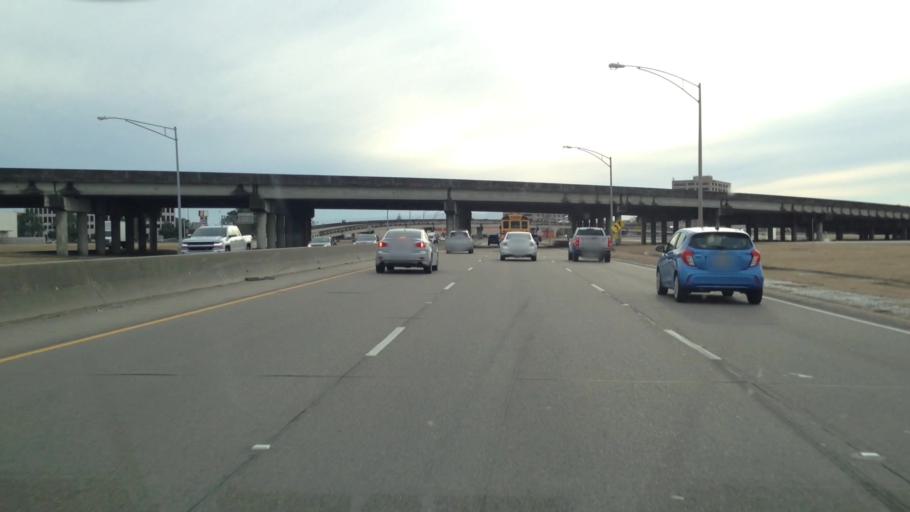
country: US
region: Louisiana
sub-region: Jefferson Parish
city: Elmwood
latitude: 29.9691
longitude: -90.1823
